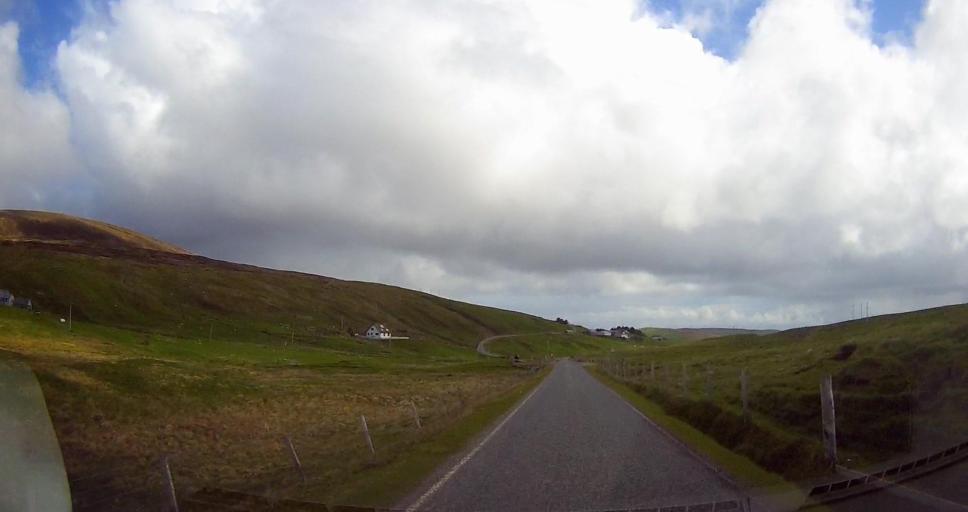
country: GB
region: Scotland
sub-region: Shetland Islands
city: Lerwick
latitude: 60.5219
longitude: -1.3759
